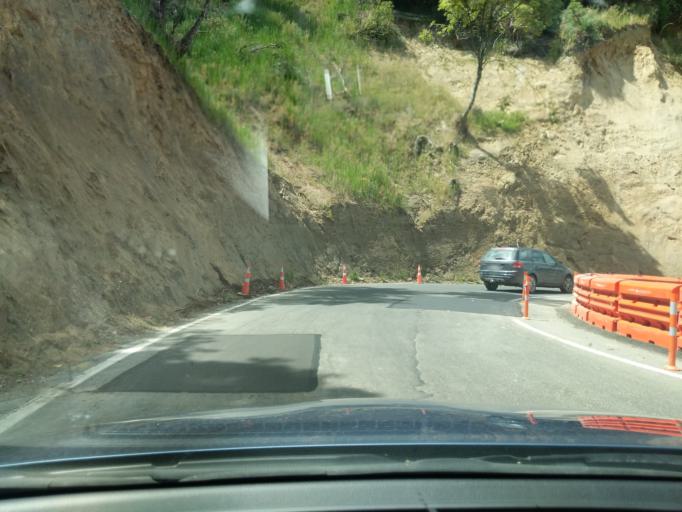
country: NZ
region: Tasman
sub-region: Tasman District
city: Motueka
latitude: -41.0474
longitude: 172.9573
